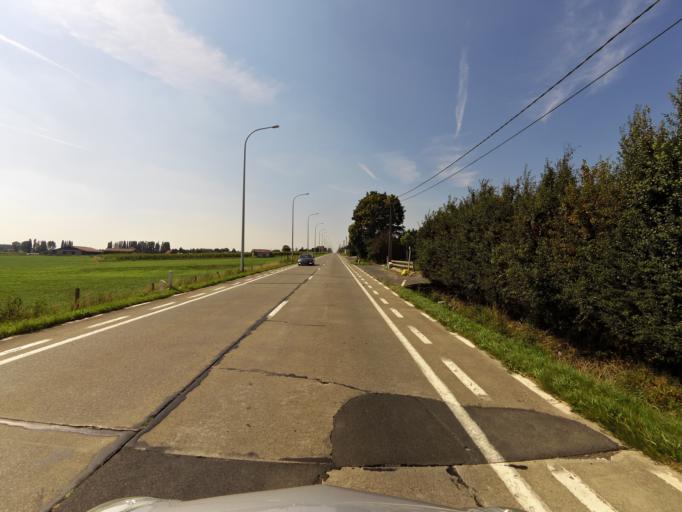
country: BE
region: Flanders
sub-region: Provincie West-Vlaanderen
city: Dentergem
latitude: 50.9907
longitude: 3.4341
